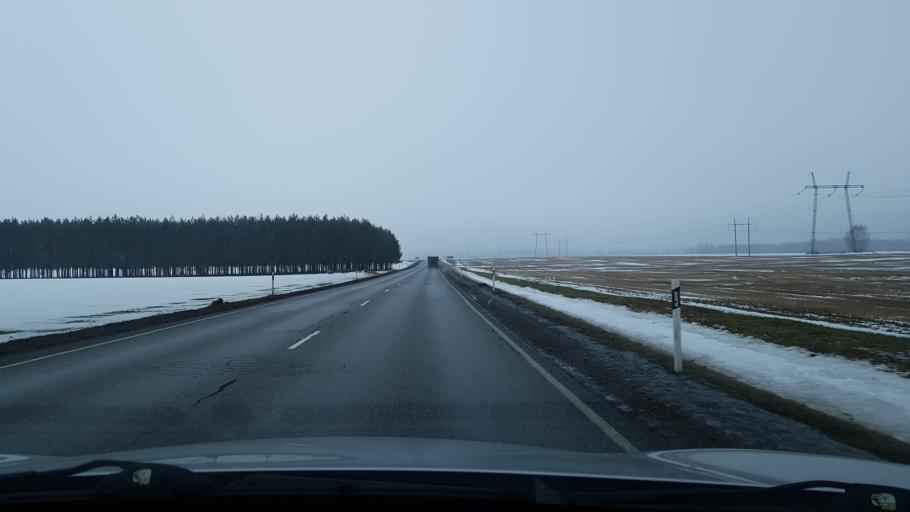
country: EE
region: Valgamaa
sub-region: Valga linn
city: Valga
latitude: 57.9467
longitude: 26.1688
